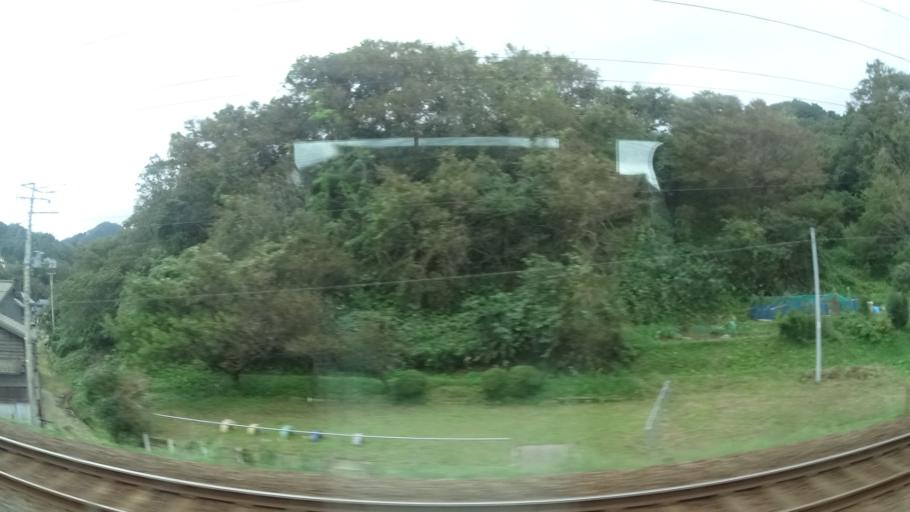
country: JP
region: Niigata
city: Murakami
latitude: 38.3679
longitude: 139.4557
